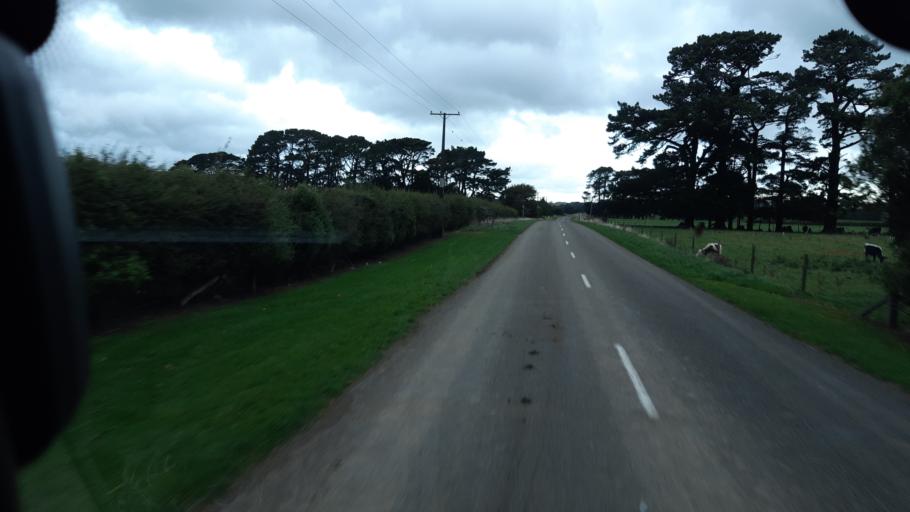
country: NZ
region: Manawatu-Wanganui
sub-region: Palmerston North City
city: Palmerston North
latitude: -40.6117
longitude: 175.6440
